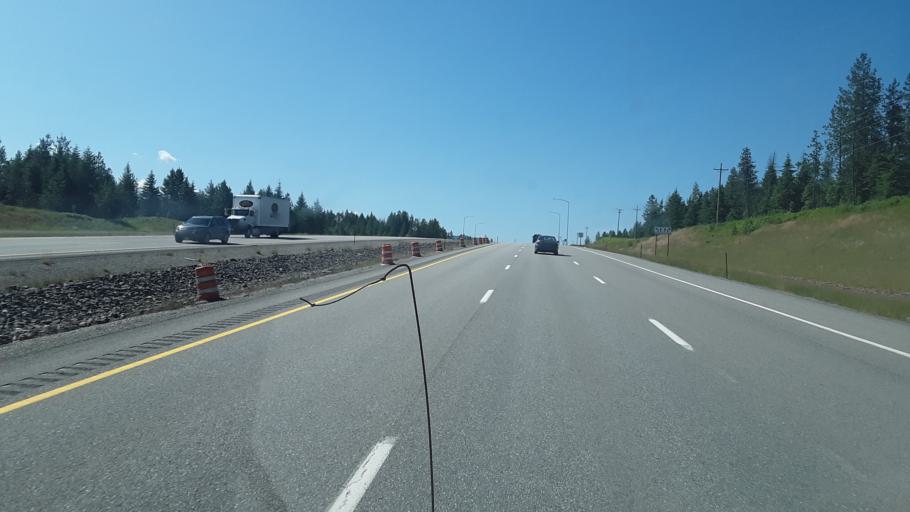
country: US
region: Idaho
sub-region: Kootenai County
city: Spirit Lake
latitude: 47.9819
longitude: -116.6987
